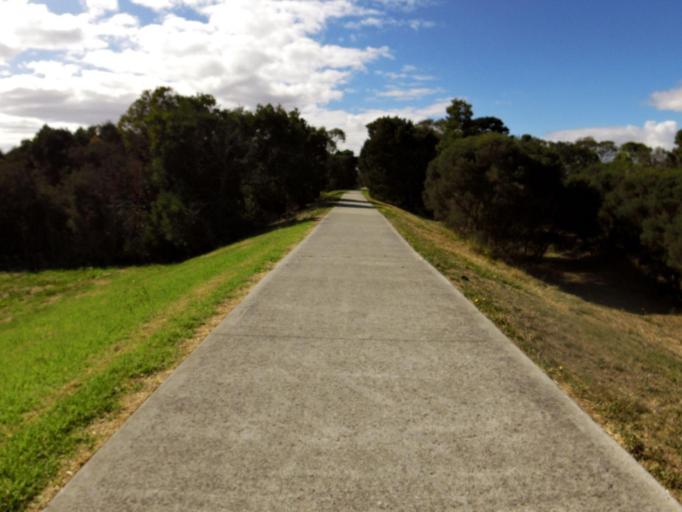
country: AU
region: Victoria
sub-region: Cardinia
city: Koo-Wee-Rup
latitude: -38.2019
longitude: 145.4942
